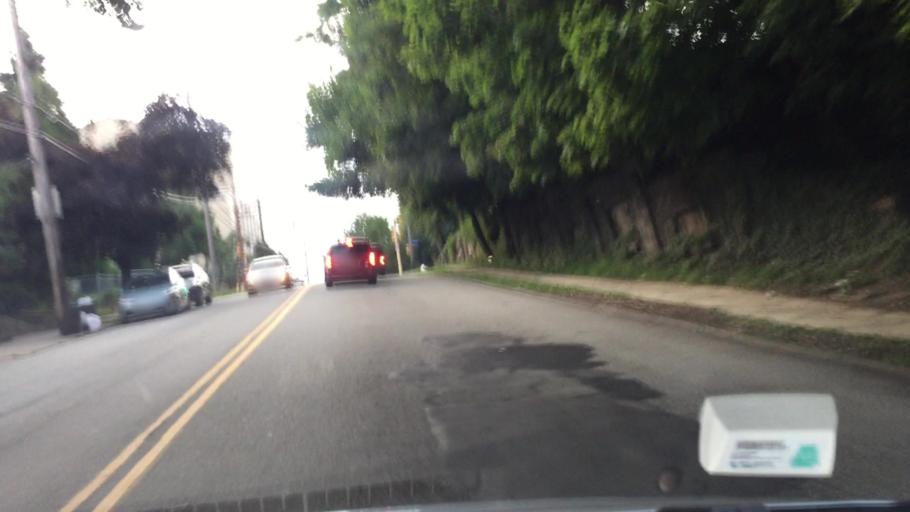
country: US
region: Pennsylvania
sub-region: Allegheny County
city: Homestead
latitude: 40.4346
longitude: -79.9187
